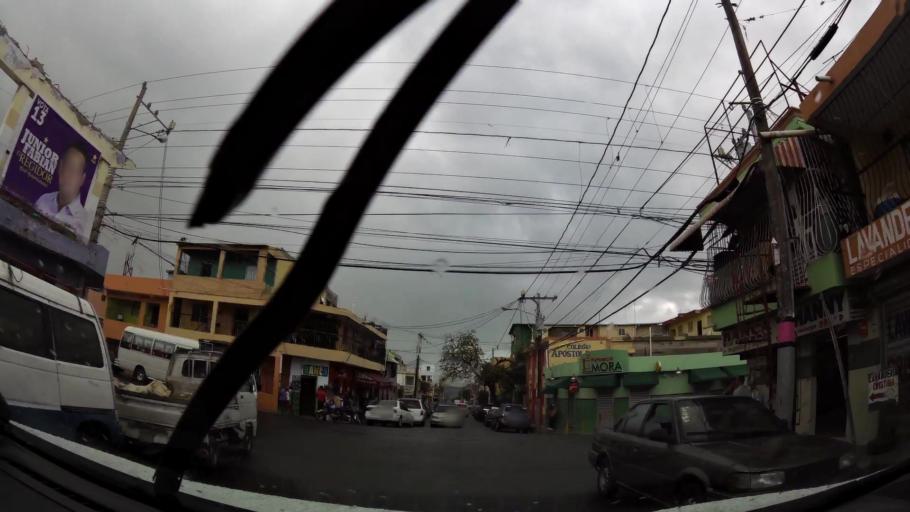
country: DO
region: Nacional
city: La Agustina
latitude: 18.5013
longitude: -69.9188
